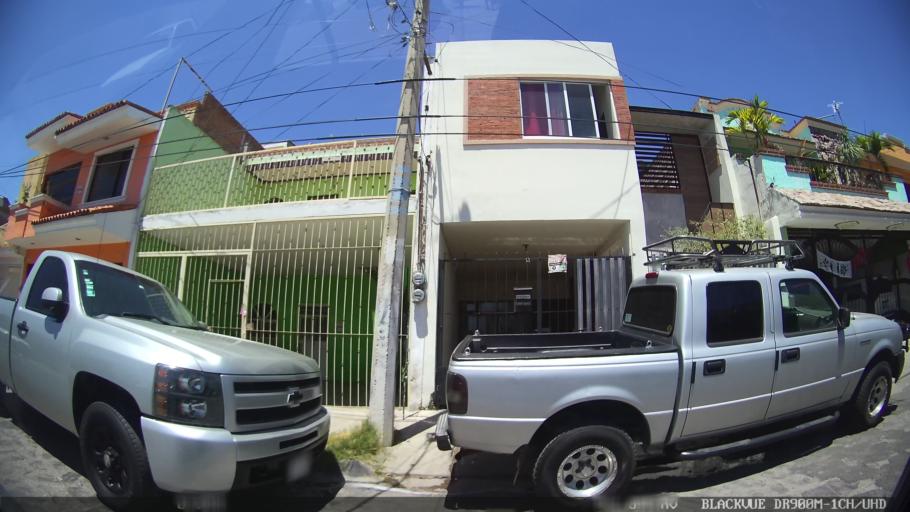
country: MX
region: Jalisco
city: Tlaquepaque
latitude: 20.6836
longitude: -103.2786
